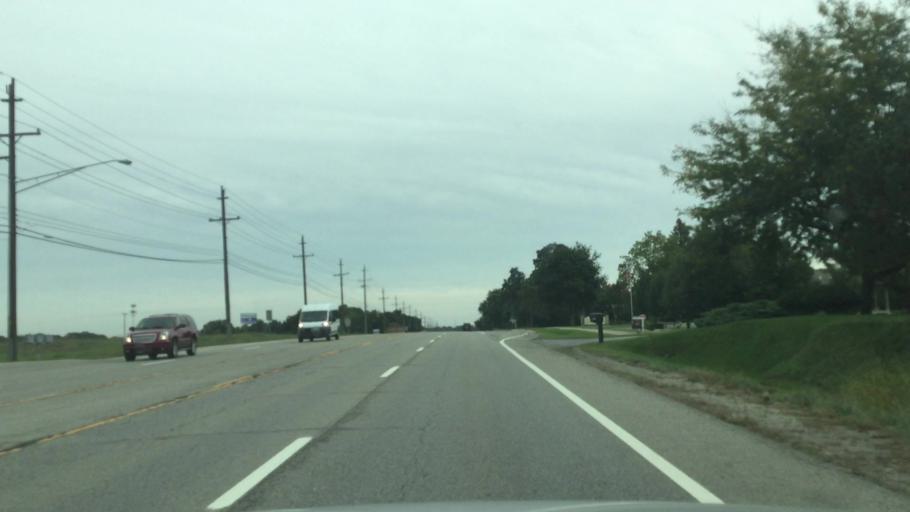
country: US
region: Michigan
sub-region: Oakland County
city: Clarkston
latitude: 42.7464
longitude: -83.4669
